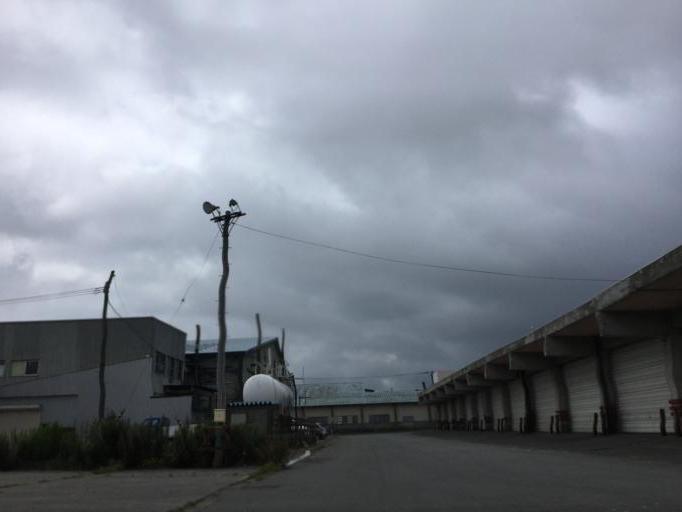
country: JP
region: Hokkaido
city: Wakkanai
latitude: 45.4076
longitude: 141.6797
